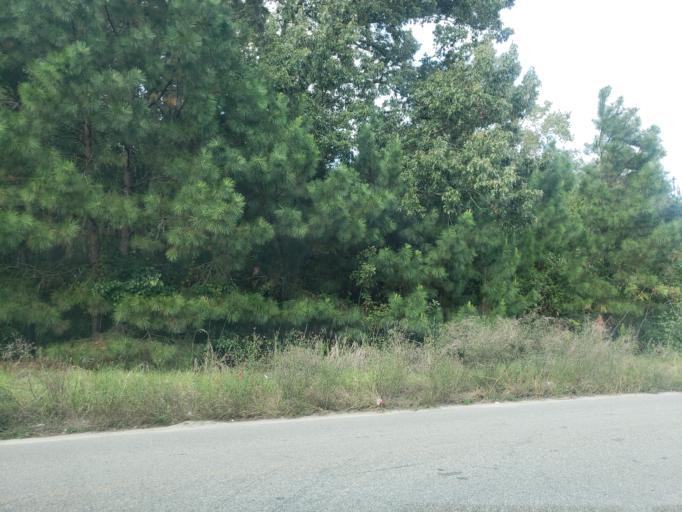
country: US
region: Georgia
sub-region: Chatham County
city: Georgetown
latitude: 32.0071
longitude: -81.2853
